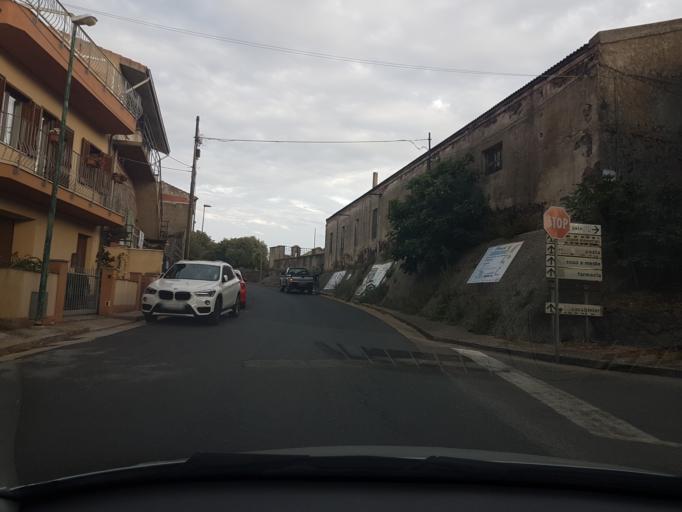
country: IT
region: Sardinia
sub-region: Provincia di Oristano
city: Seneghe
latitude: 40.0826
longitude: 8.6080
